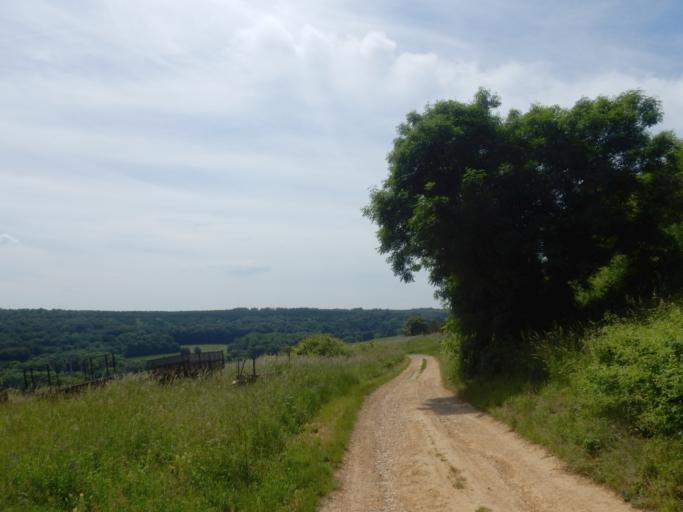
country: FR
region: Lorraine
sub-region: Departement de Meurthe-et-Moselle
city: Pagny-sur-Moselle
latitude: 48.9762
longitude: 5.9885
